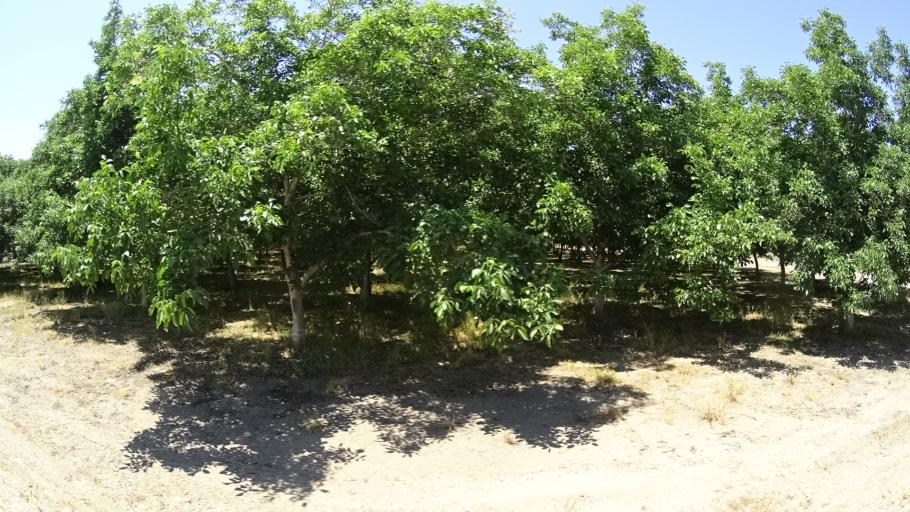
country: US
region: California
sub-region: Kings County
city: Lucerne
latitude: 36.4264
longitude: -119.6010
